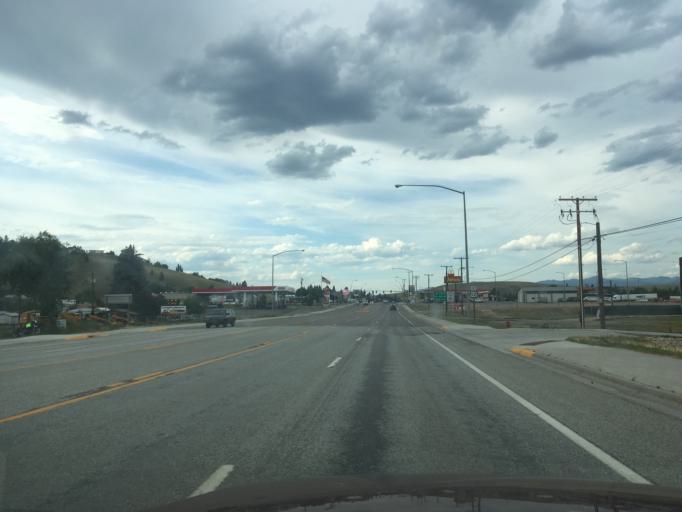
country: US
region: Montana
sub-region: Missoula County
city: Lolo
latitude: 46.7542
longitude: -114.0824
